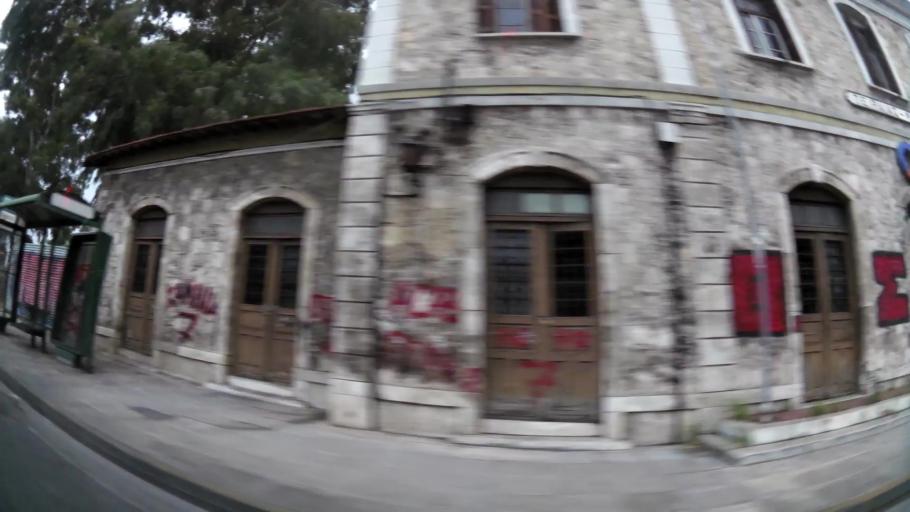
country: GR
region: Attica
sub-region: Nomos Attikis
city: Piraeus
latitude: 37.9484
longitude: 23.6358
